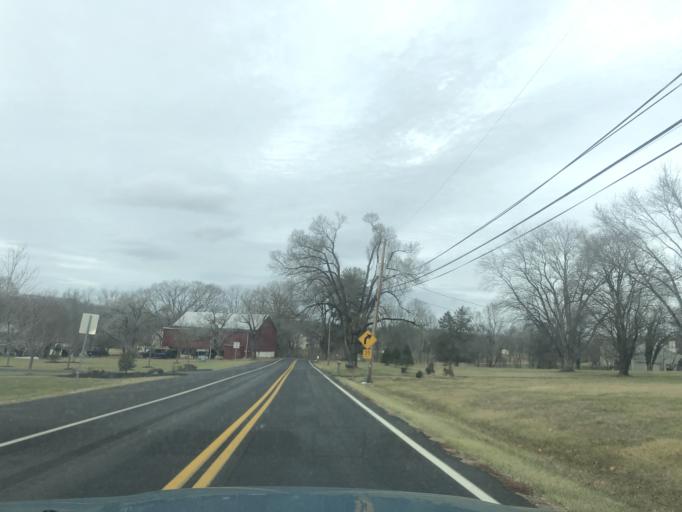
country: US
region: Pennsylvania
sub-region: Montgomery County
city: Harleysville
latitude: 40.2671
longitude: -75.4135
